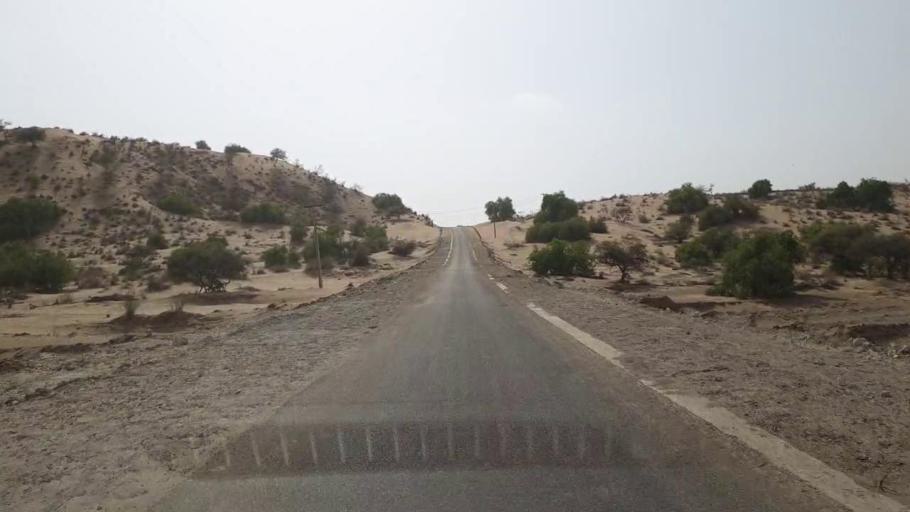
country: PK
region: Sindh
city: Mithi
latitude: 24.6210
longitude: 69.9138
